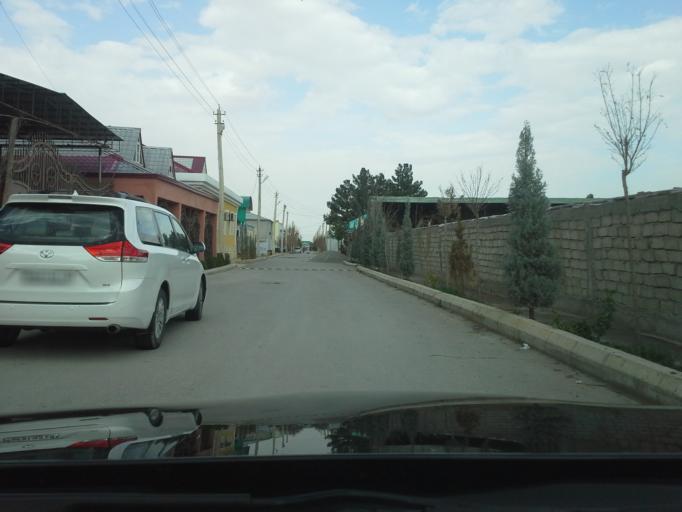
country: TM
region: Ahal
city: Abadan
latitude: 37.9884
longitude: 58.2800
